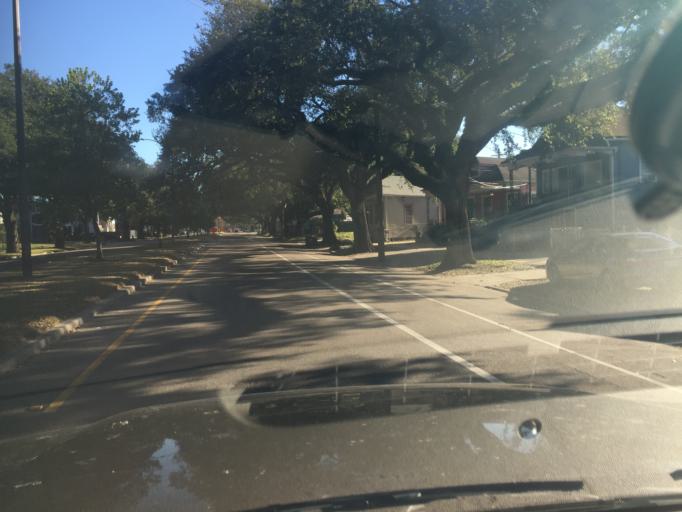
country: US
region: Louisiana
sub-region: Orleans Parish
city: New Orleans
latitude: 29.9810
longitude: -90.0705
